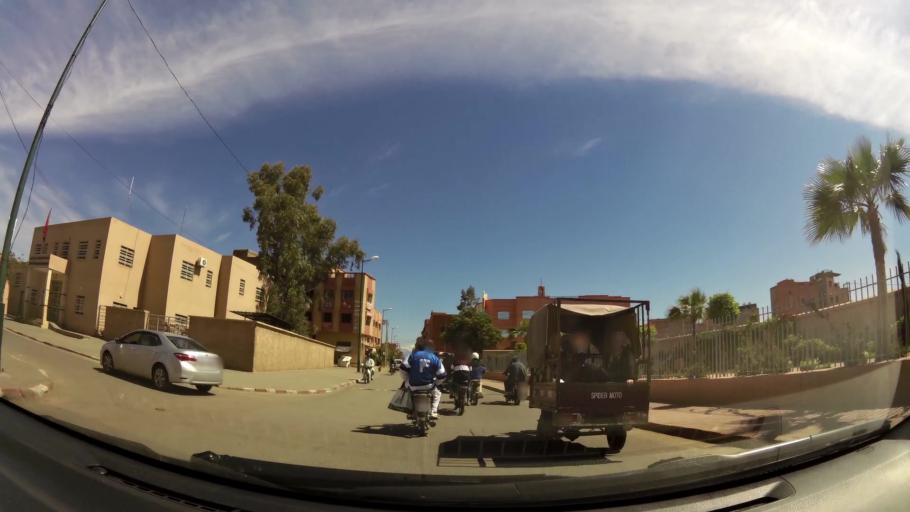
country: MA
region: Marrakech-Tensift-Al Haouz
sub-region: Marrakech
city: Marrakesh
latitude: 31.6001
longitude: -7.9616
